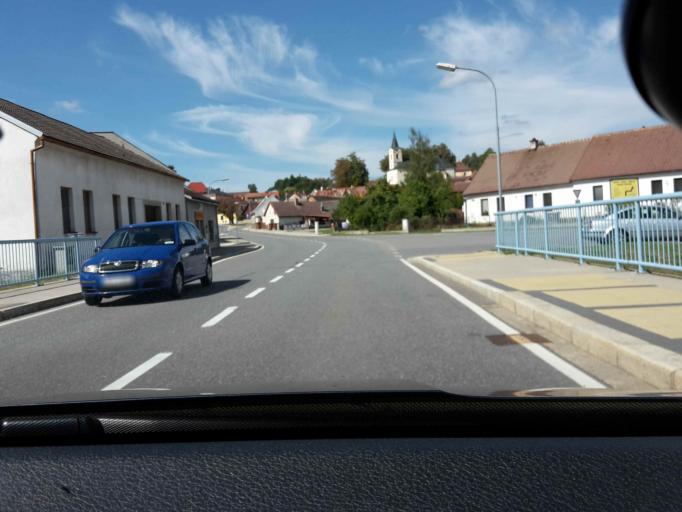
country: CZ
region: Vysocina
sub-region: Okres Jihlava
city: Telc
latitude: 49.1894
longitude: 15.3798
